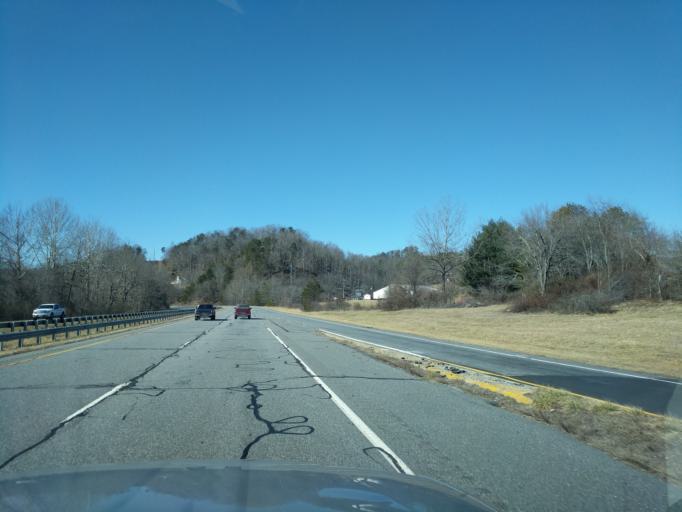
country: US
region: North Carolina
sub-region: Swain County
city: Cherokee
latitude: 35.4211
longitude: -83.3350
